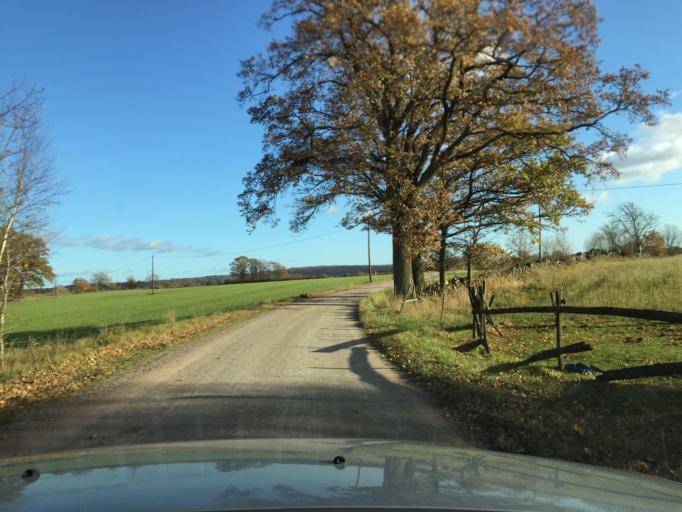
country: SE
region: Skane
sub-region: Hassleholms Kommun
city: Tormestorp
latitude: 56.0681
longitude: 13.7135
